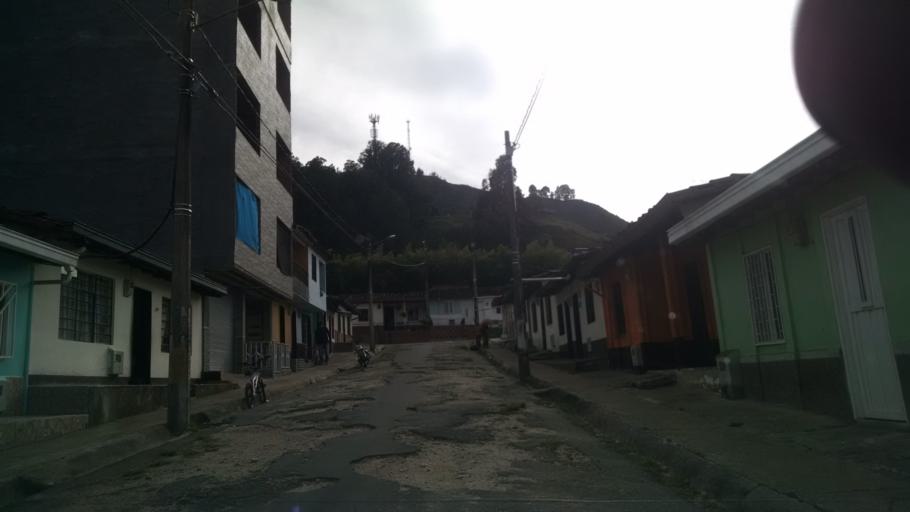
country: CO
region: Antioquia
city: Guatape
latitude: 6.2151
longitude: -75.2397
